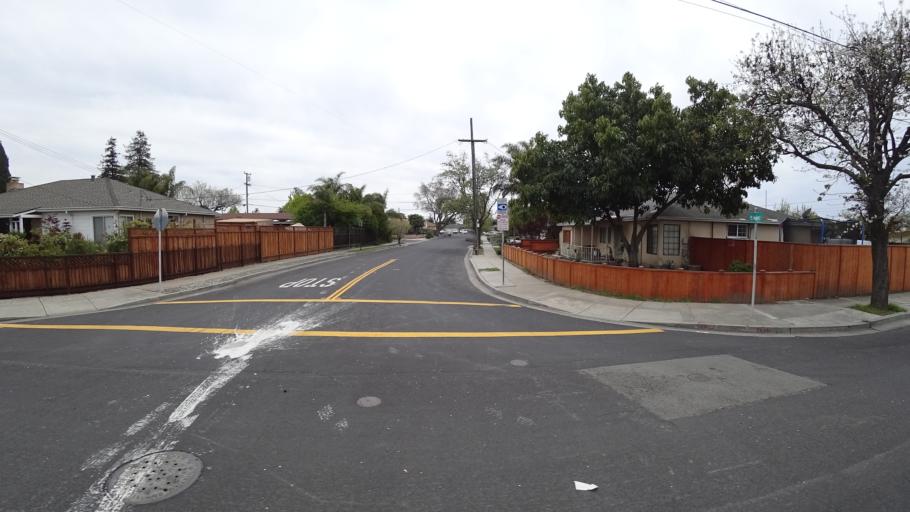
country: US
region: California
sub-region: Alameda County
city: Hayward
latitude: 37.6497
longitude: -122.0744
